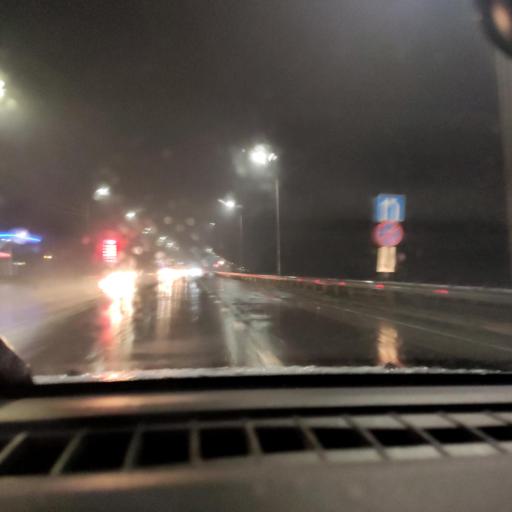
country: RU
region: Voronezj
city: Devitsa
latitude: 51.6323
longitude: 38.9869
